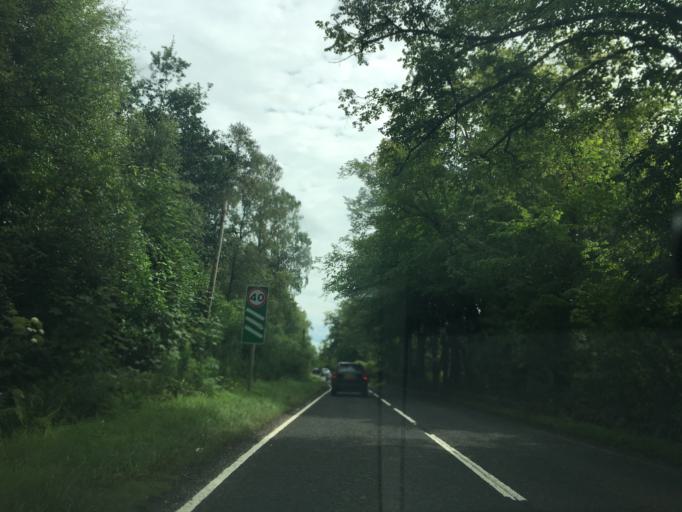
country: GB
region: Scotland
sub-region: Stirling
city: Callander
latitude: 56.2502
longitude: -4.2594
